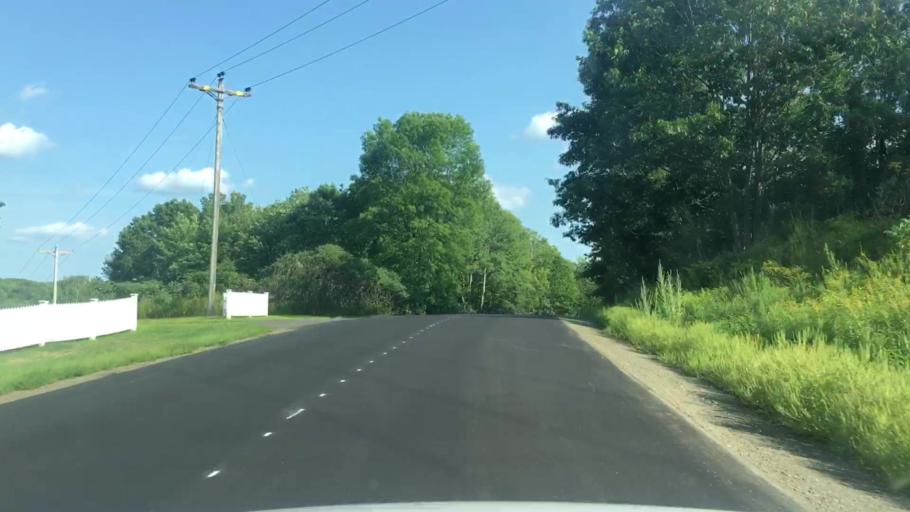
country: US
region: Maine
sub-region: Kennebec County
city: Waterville
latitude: 44.5761
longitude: -69.6600
